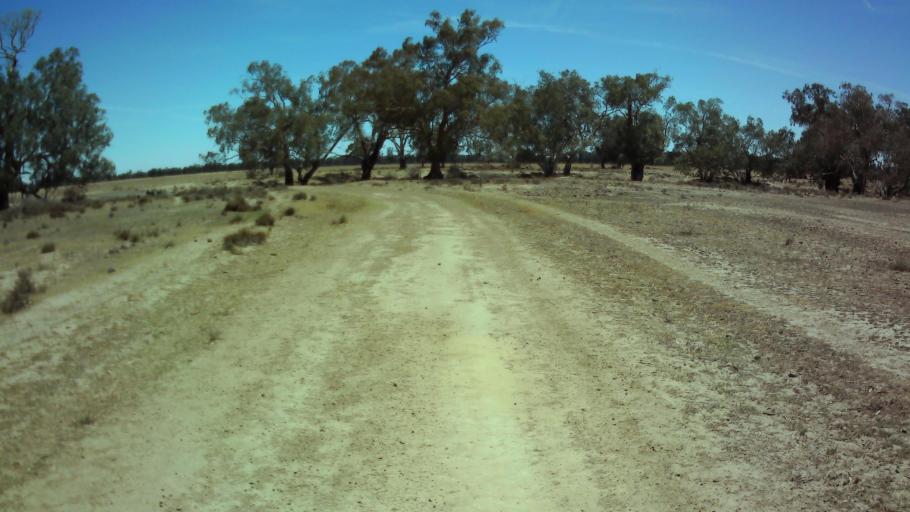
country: AU
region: New South Wales
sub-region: Bland
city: West Wyalong
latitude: -33.8362
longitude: 147.6333
